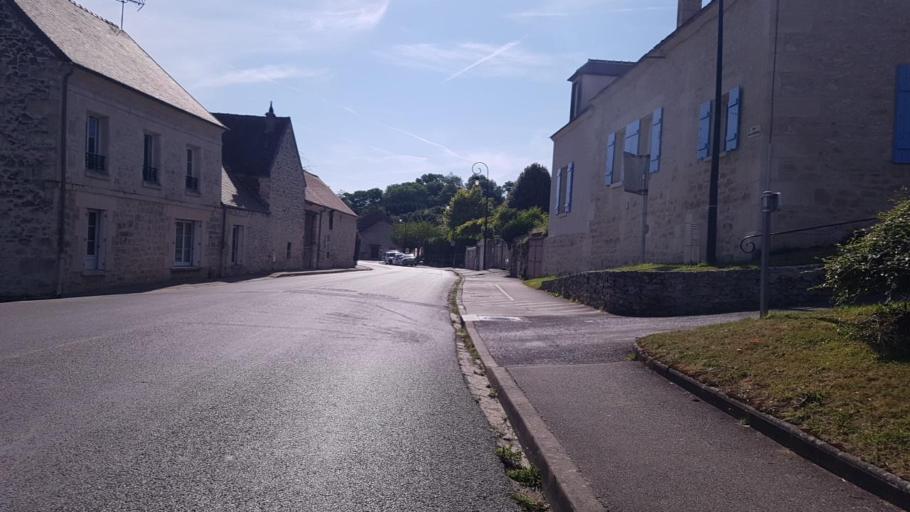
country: FR
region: Picardie
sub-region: Departement de l'Oise
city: Pontpoint
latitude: 49.3002
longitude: 2.6403
